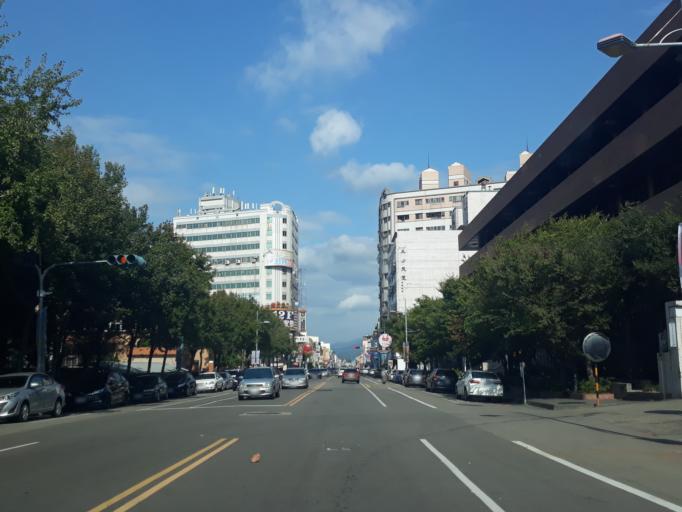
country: TW
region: Taiwan
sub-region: Miaoli
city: Miaoli
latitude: 24.5711
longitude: 120.8285
